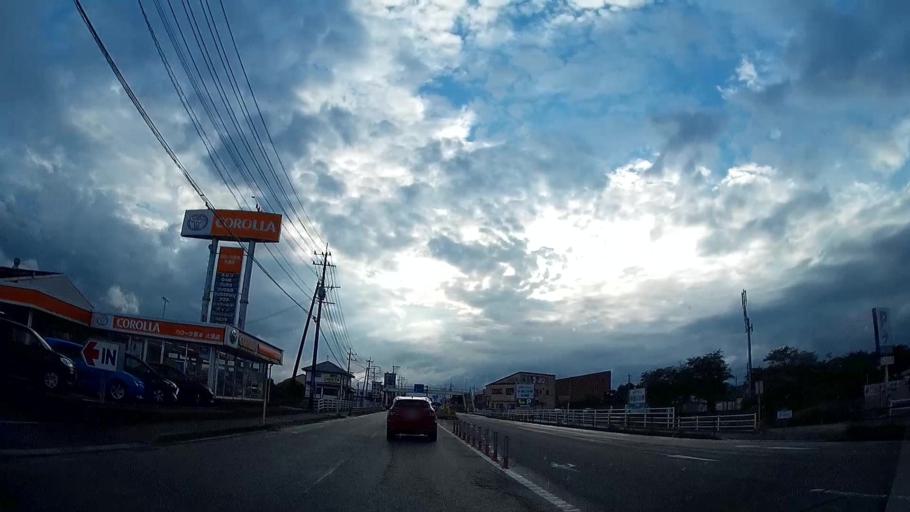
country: JP
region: Kumamoto
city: Ozu
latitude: 32.8755
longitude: 130.8780
